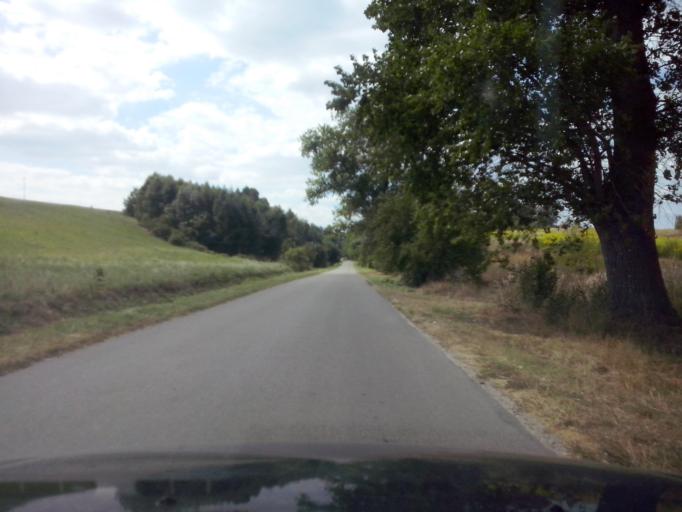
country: PL
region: Swietokrzyskie
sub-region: Powiat staszowski
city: Staszow
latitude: 50.5693
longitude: 21.1330
